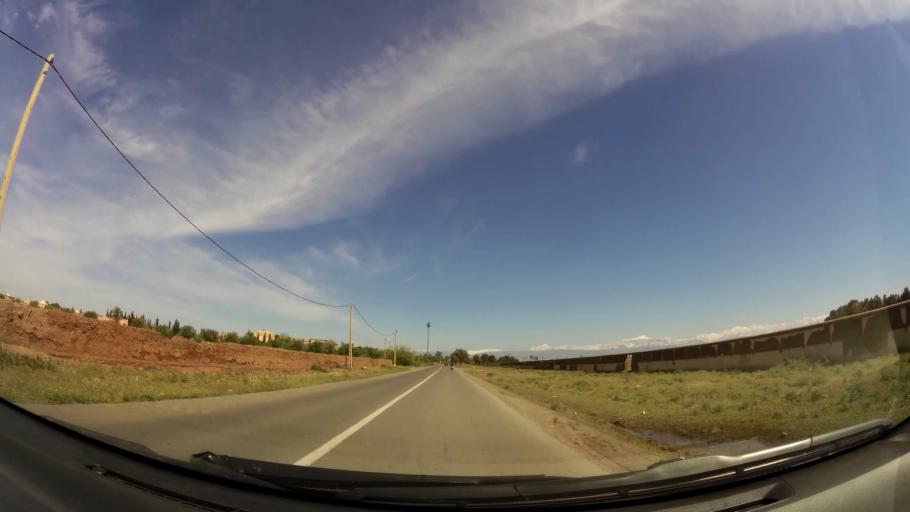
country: MA
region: Marrakech-Tensift-Al Haouz
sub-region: Marrakech
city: Marrakesh
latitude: 31.6125
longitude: -7.9441
